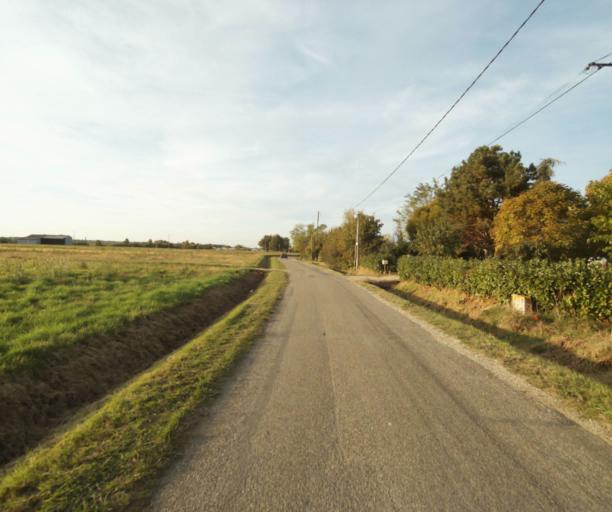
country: FR
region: Midi-Pyrenees
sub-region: Departement du Tarn-et-Garonne
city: Campsas
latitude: 43.8764
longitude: 1.3498
